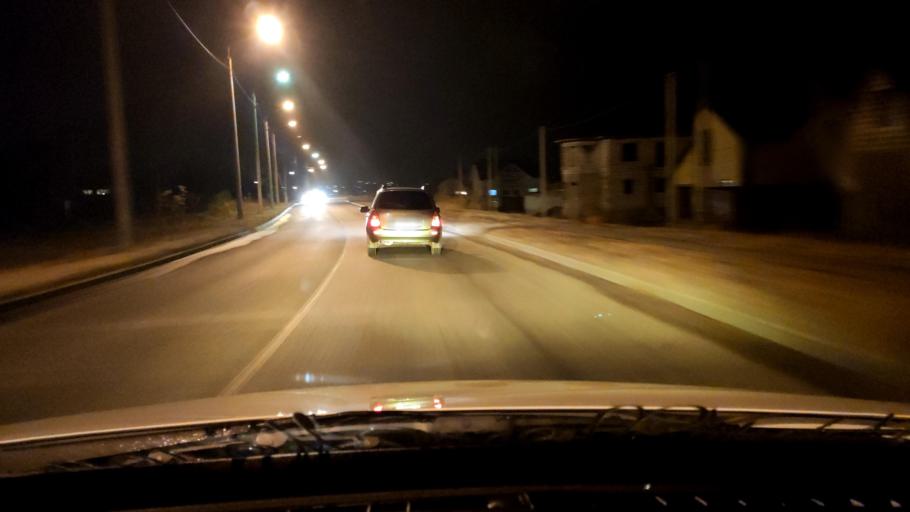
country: RU
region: Voronezj
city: Semiluki
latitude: 51.6632
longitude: 39.0402
